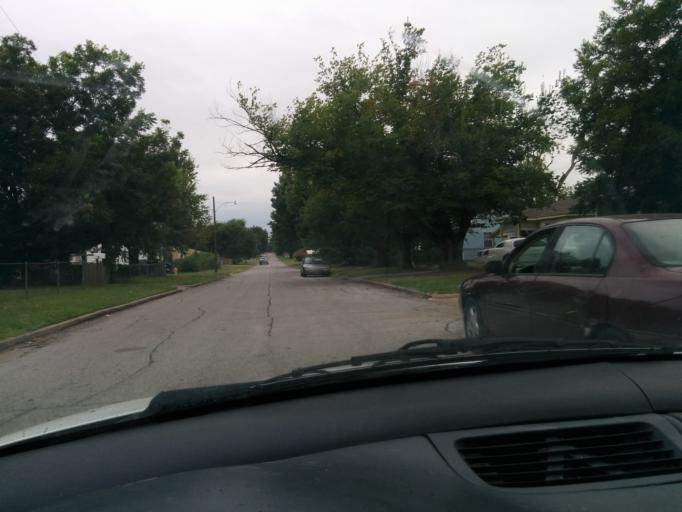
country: US
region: Oklahoma
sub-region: Tulsa County
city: Tulsa
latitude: 36.1680
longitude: -95.9064
